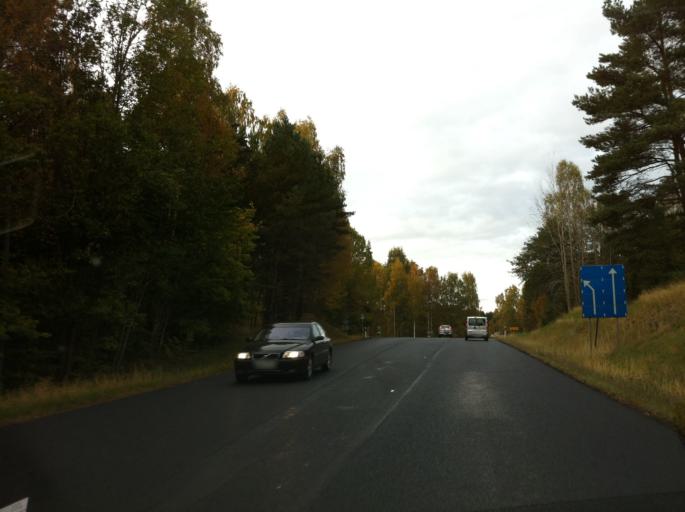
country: SE
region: OEstergoetland
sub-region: Motala Kommun
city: Ryd
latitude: 58.6959
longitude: 14.9677
